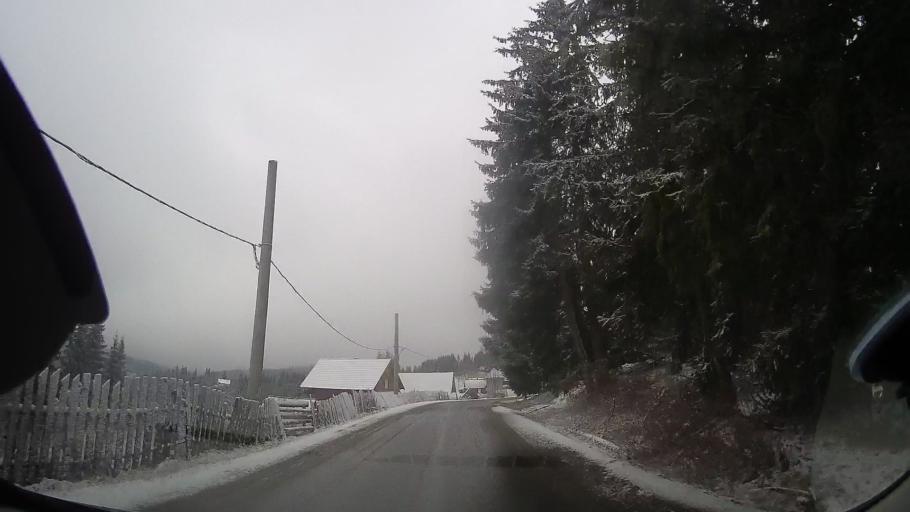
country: RO
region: Cluj
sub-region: Comuna Maguri-Racatau
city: Maguri
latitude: 46.6469
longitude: 23.0770
